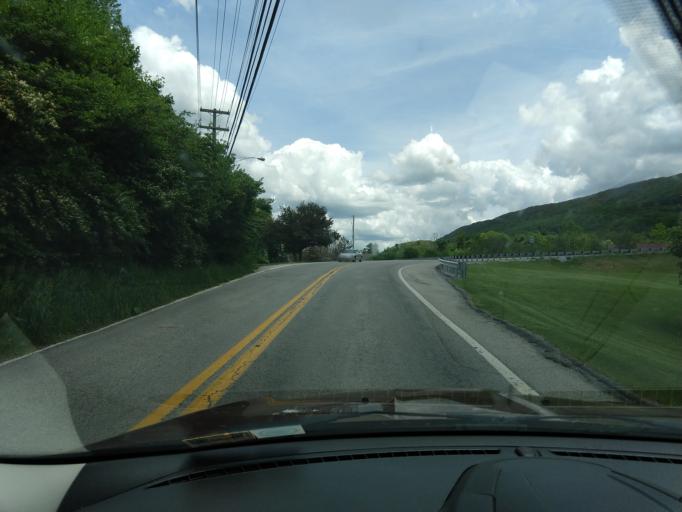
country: US
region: West Virginia
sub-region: Mercer County
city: Bluefield
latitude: 37.2456
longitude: -81.2279
